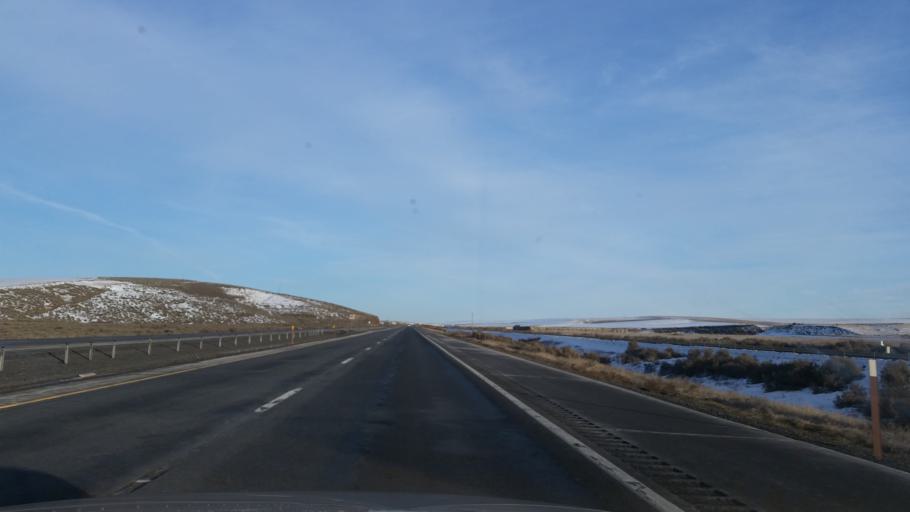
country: US
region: Washington
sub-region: Grant County
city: Warden
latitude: 47.0847
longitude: -118.9939
